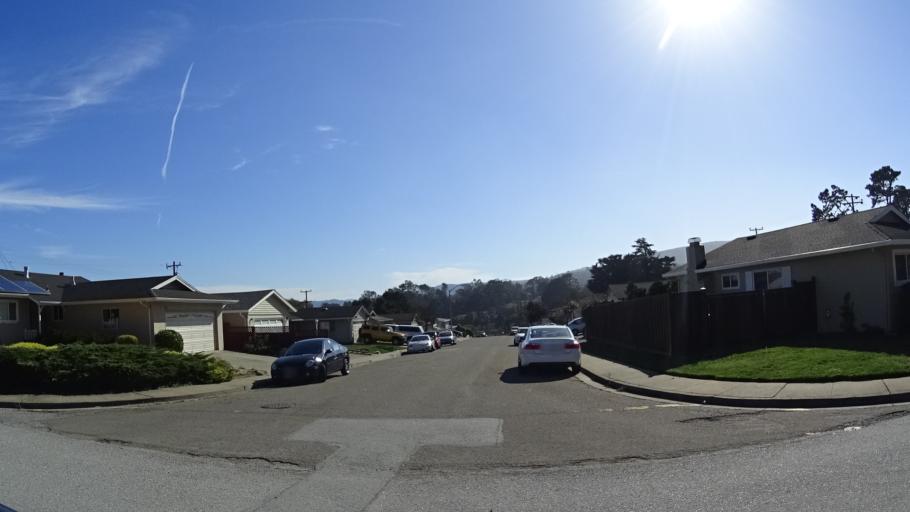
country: US
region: California
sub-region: San Mateo County
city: San Bruno
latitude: 37.6346
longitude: -122.4481
